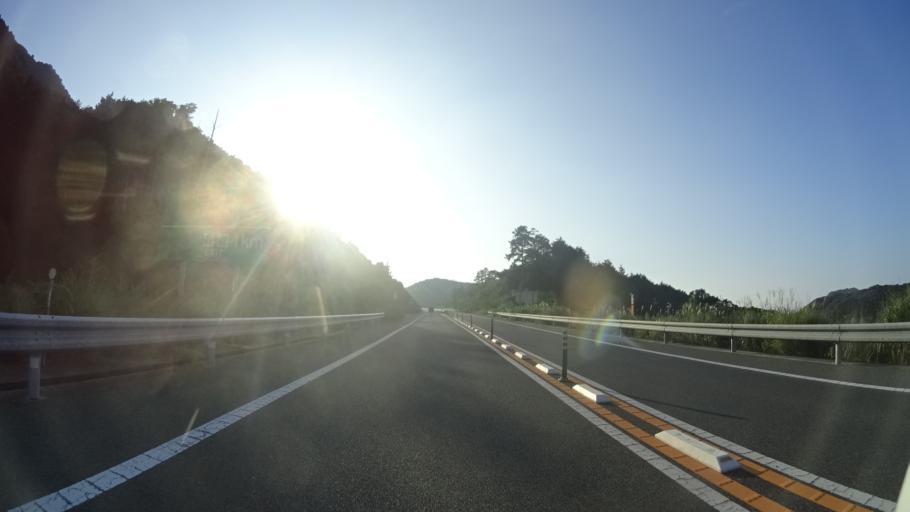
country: JP
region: Yamaguchi
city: Hagi
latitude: 34.3881
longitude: 131.3371
